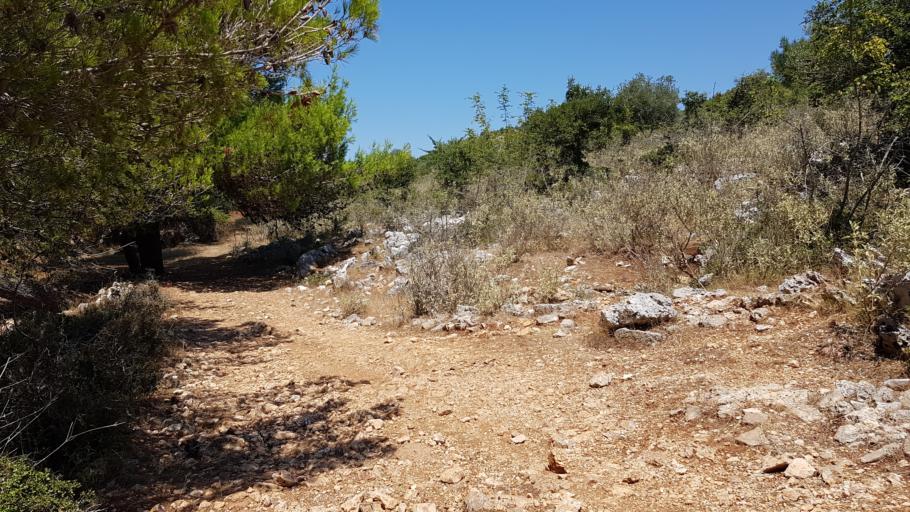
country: AL
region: Vlore
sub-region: Rrethi i Sarandes
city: Xarre
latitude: 39.7556
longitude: 19.9957
